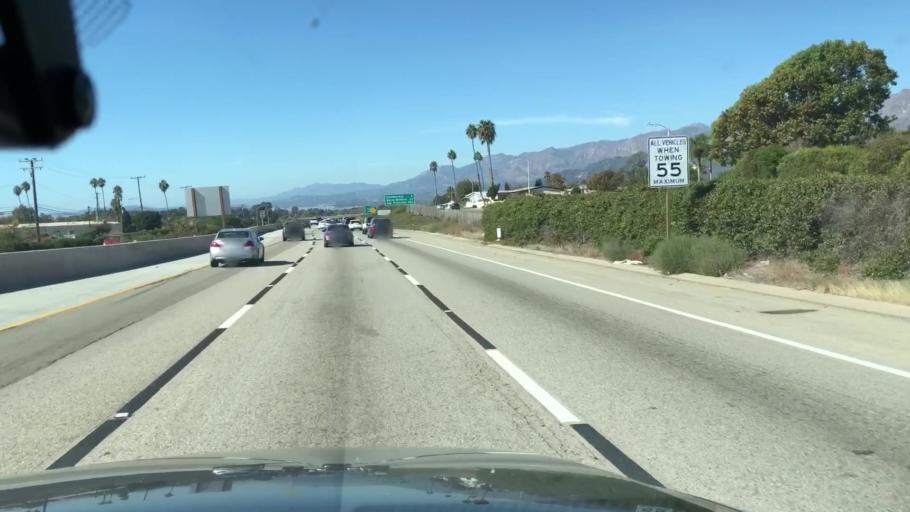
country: US
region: California
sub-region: Santa Barbara County
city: Carpinteria
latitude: 34.3863
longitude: -119.4912
